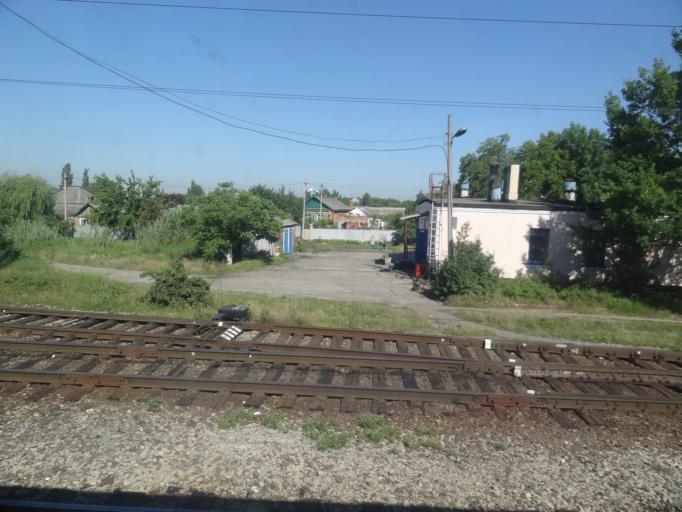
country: RU
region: Adygeya
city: Enem
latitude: 44.9305
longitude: 38.9086
